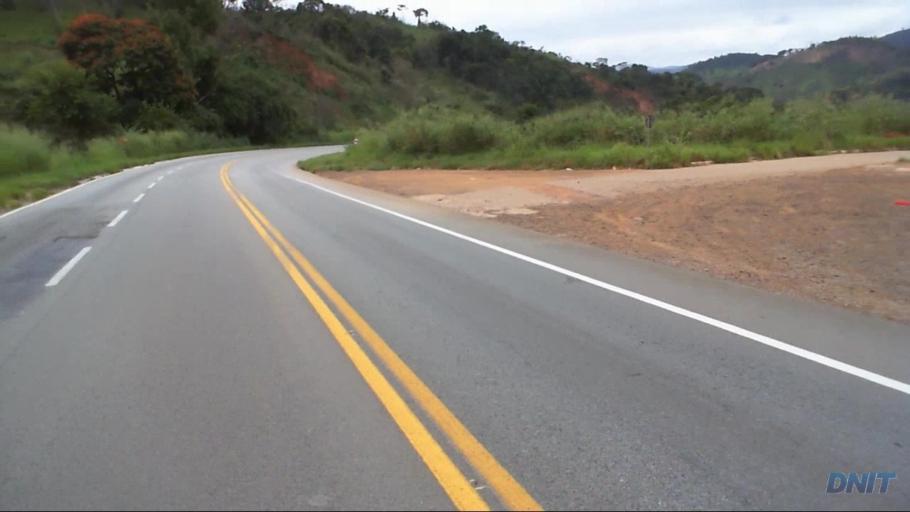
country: BR
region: Minas Gerais
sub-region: Nova Era
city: Nova Era
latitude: -19.7882
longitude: -43.0523
